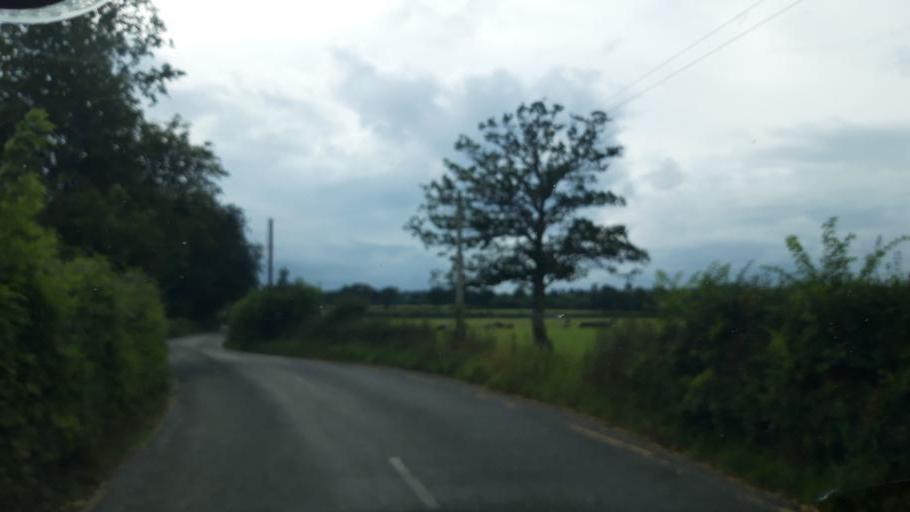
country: IE
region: Leinster
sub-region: Kilkenny
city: Ballyragget
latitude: 52.7574
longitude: -7.3861
